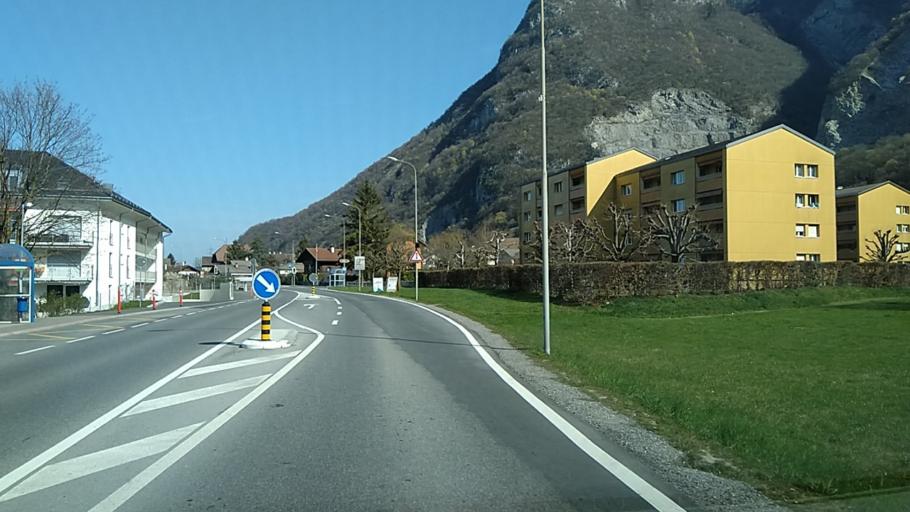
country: CH
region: Vaud
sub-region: Aigle District
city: Villeneuve
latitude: 46.3567
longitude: 6.9320
